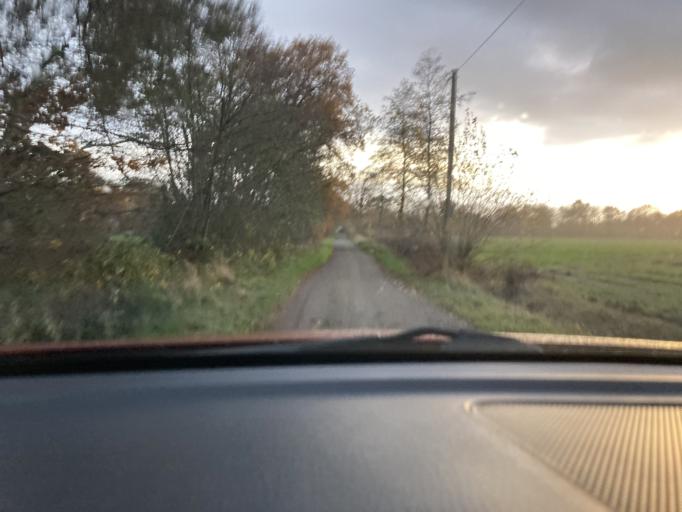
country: DE
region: Lower Saxony
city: Ritterhude
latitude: 53.1914
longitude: 8.6956
